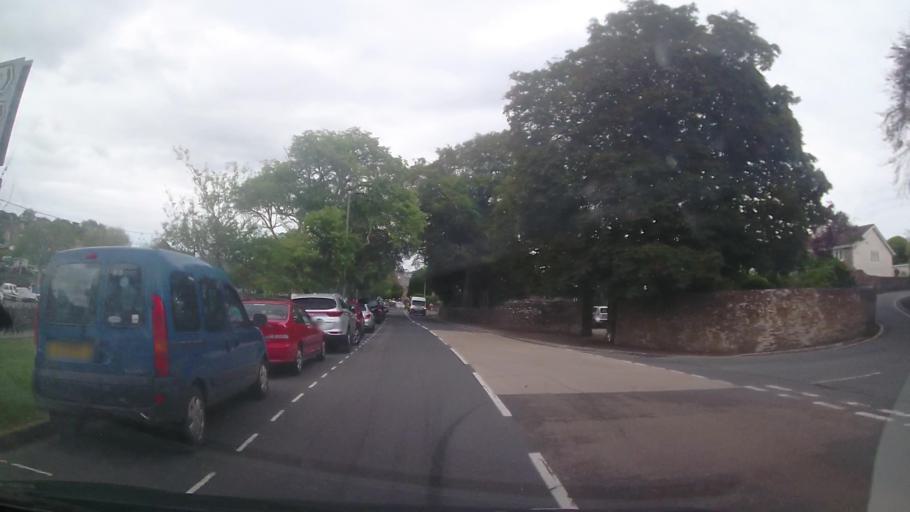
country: GB
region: England
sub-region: Devon
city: Kingsbridge
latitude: 50.2812
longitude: -3.7748
